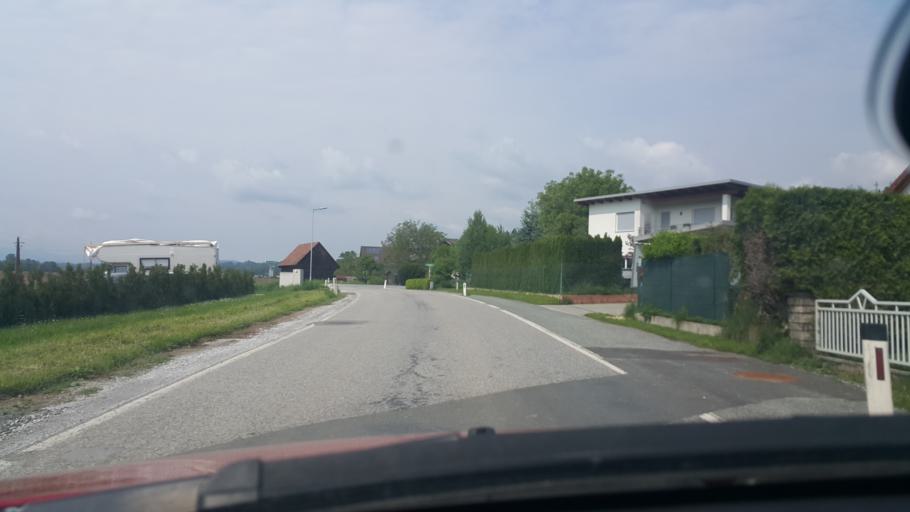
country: AT
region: Styria
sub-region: Politischer Bezirk Graz-Umgebung
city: Lieboch
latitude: 46.9790
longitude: 15.3418
